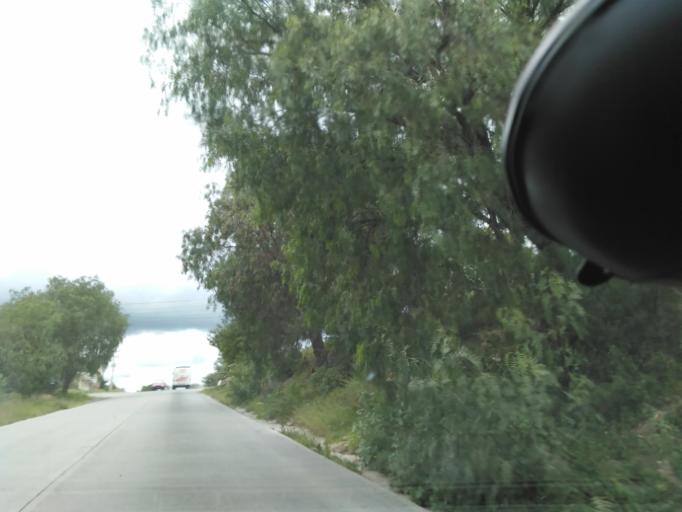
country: MX
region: Hidalgo
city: Tula de Allende
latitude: 20.0594
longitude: -99.3554
